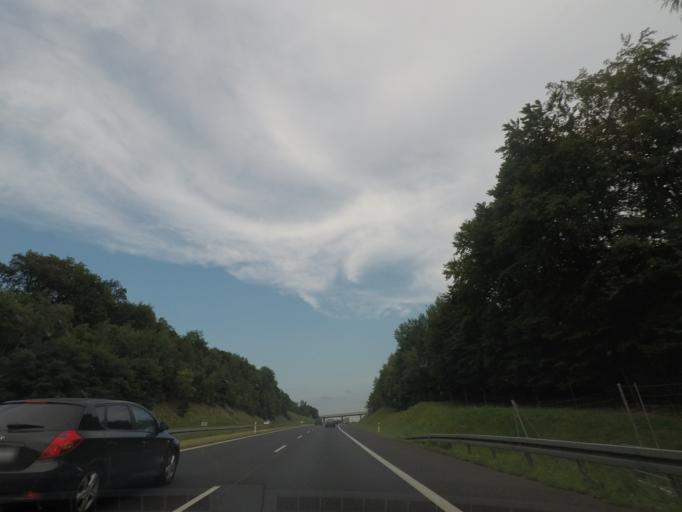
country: PL
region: Lesser Poland Voivodeship
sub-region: Powiat krakowski
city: Czulow
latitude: 50.0922
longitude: 19.6834
